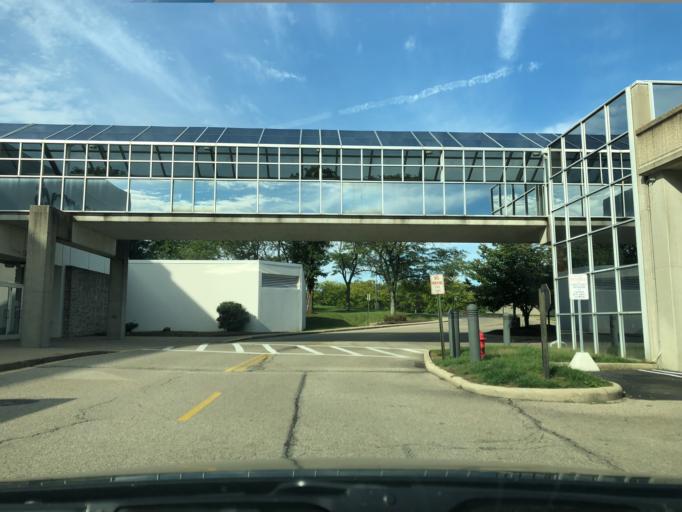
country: US
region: Ohio
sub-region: Hamilton County
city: Springdale
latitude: 39.2924
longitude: -84.4642
